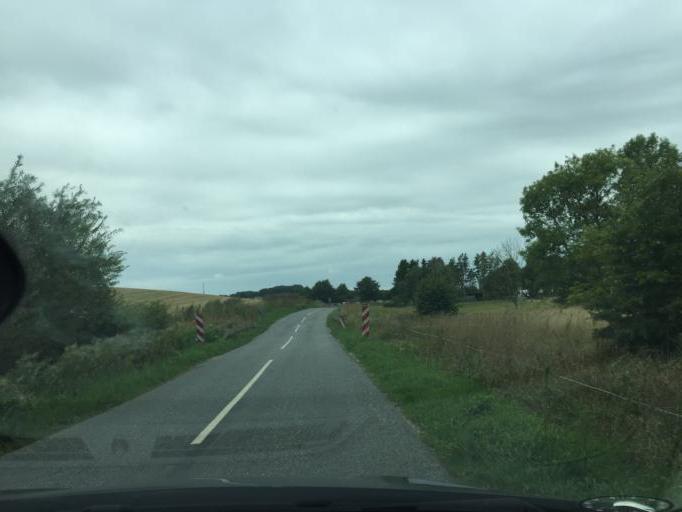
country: DK
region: South Denmark
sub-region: Assens Kommune
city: Arup
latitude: 55.3764
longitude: 10.0774
